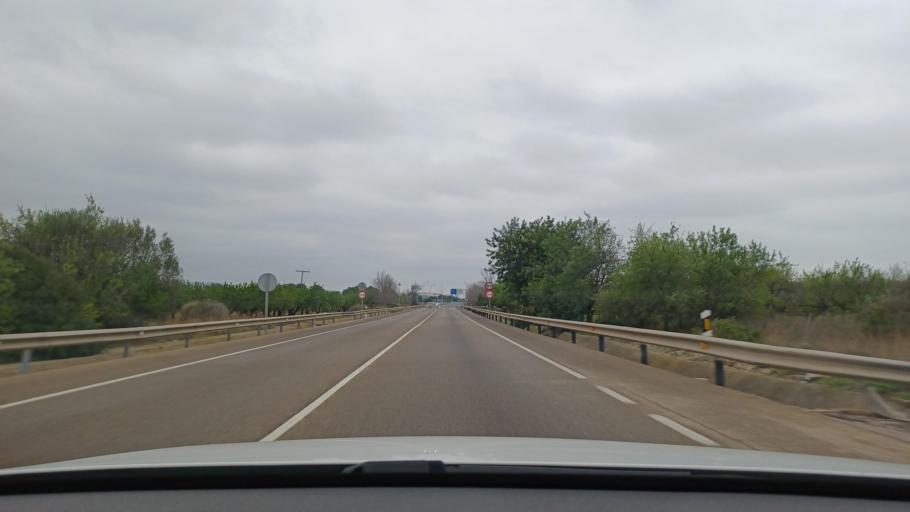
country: ES
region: Valencia
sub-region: Provincia de Castello
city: Orpesa/Oropesa del Mar
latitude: 40.1004
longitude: 0.1348
